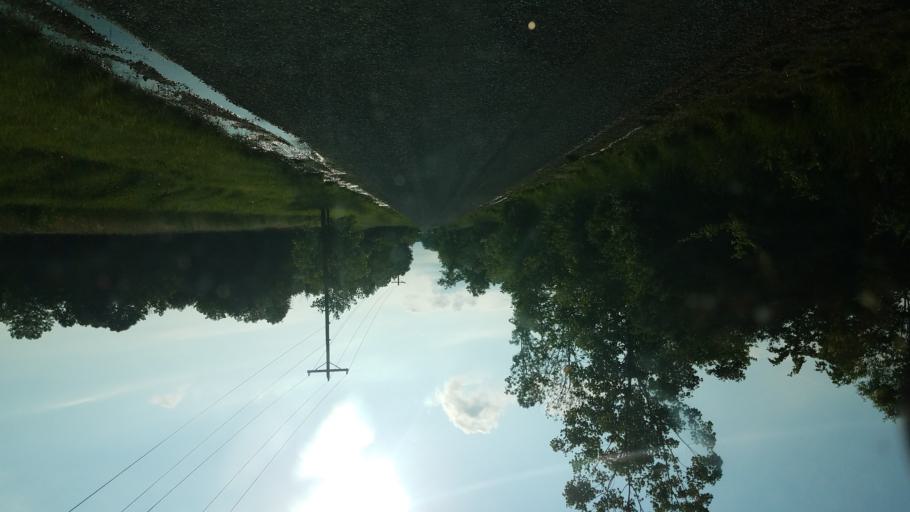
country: US
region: Ohio
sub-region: Morrow County
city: Cardington
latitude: 40.4248
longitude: -82.8117
